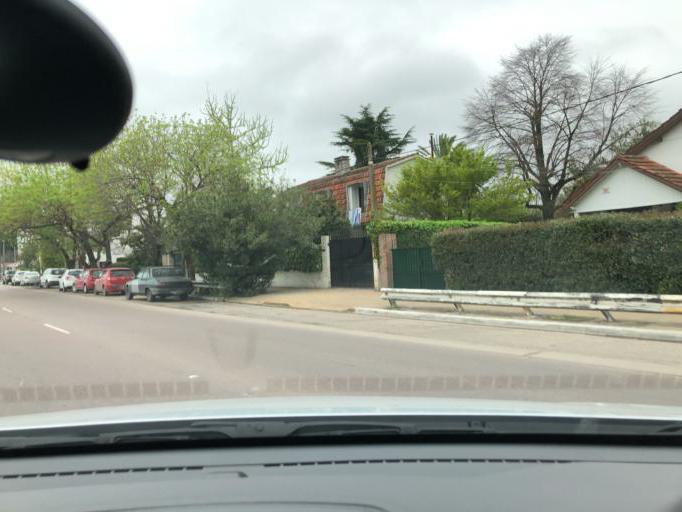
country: AR
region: Buenos Aires
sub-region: Partido de La Plata
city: La Plata
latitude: -34.8642
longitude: -58.0467
